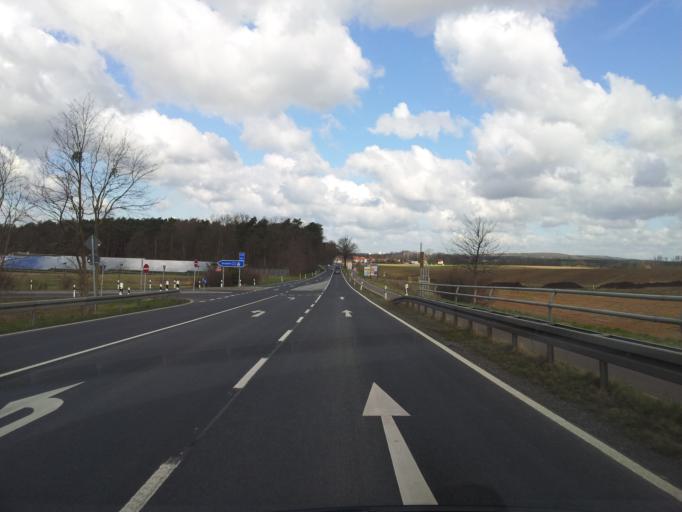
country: DE
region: Saxony
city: Ottendorf-Okrilla
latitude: 51.1728
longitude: 13.8565
